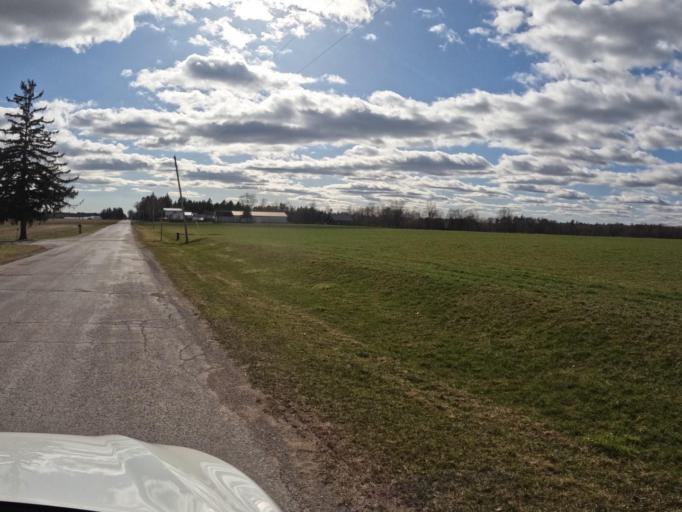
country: CA
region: Ontario
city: Norfolk County
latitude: 42.7509
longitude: -80.3857
